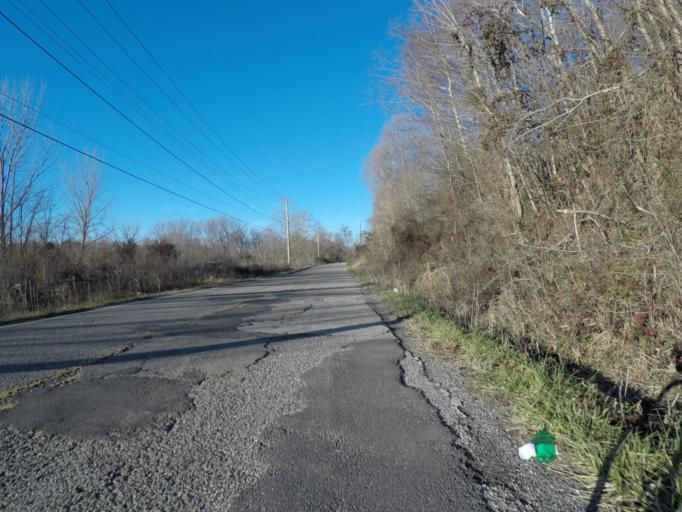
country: US
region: Kentucky
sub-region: Boyd County
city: Catlettsburg
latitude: 38.3947
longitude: -82.5932
